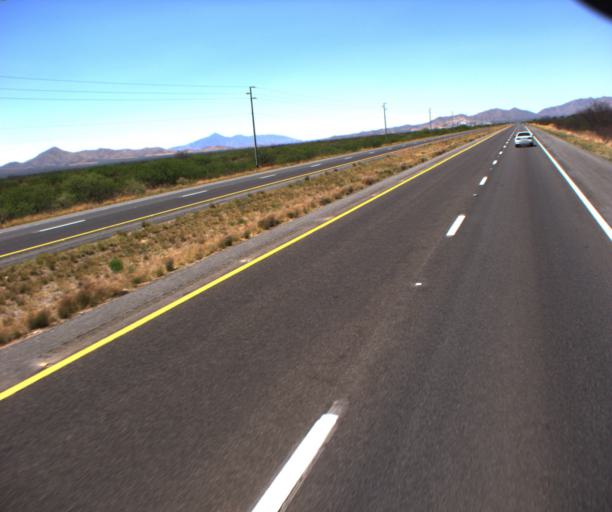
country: US
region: Arizona
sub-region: Cochise County
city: Pirtleville
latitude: 31.3612
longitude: -109.6675
